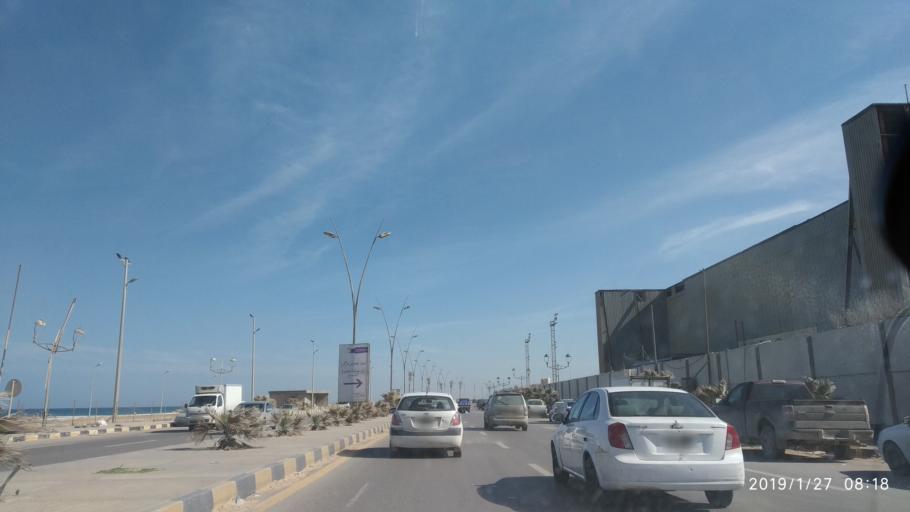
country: LY
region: Tripoli
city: Tagiura
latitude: 32.9082
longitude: 13.2747
